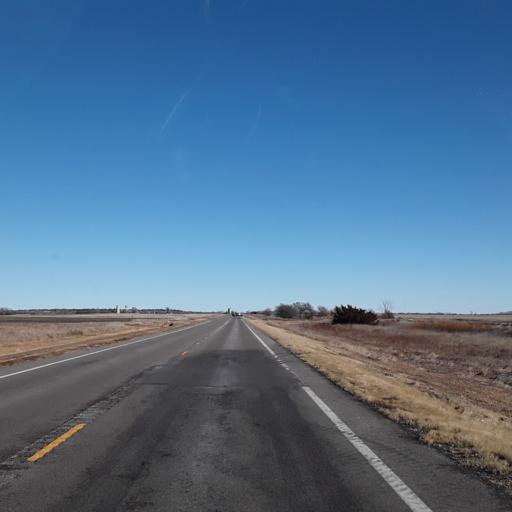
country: US
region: Kansas
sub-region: Pawnee County
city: Larned
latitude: 38.1442
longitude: -99.1443
